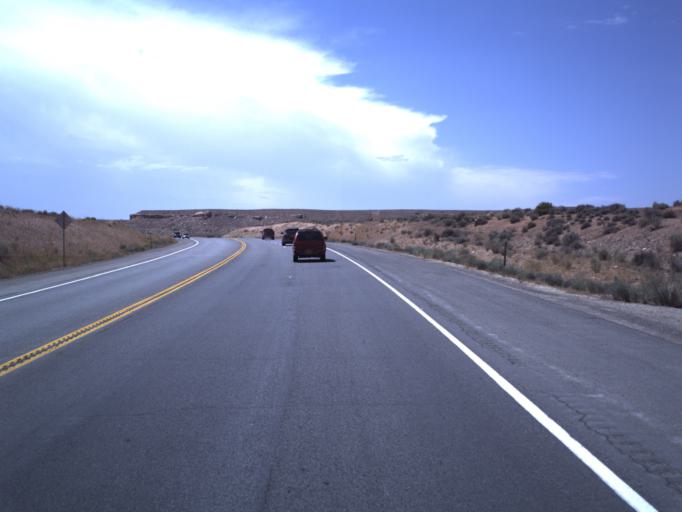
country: US
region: Utah
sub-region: Uintah County
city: Maeser
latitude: 40.3232
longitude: -109.6883
